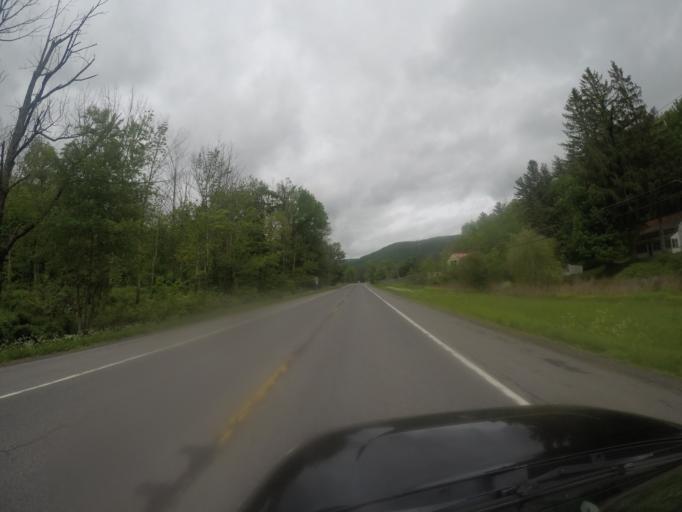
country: US
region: New York
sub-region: Ulster County
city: Shokan
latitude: 42.1185
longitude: -74.3847
